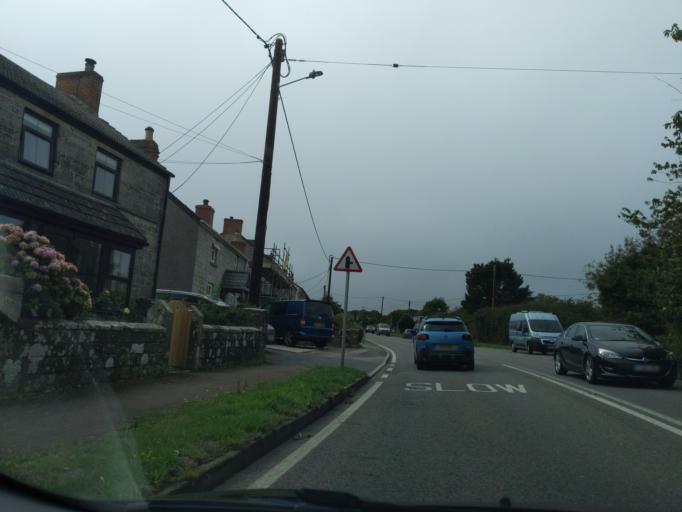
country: GB
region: England
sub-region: Cornwall
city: Porthleven
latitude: 50.1080
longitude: -5.3353
